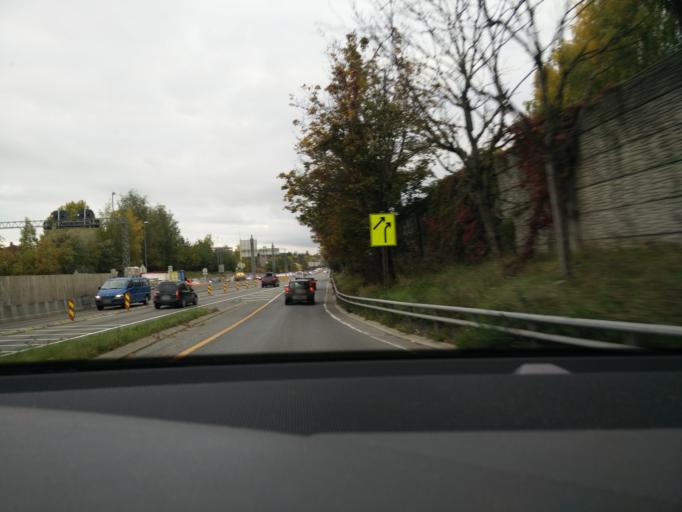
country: NO
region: Oslo
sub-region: Oslo
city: Sjolyststranda
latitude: 59.9365
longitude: 10.6790
